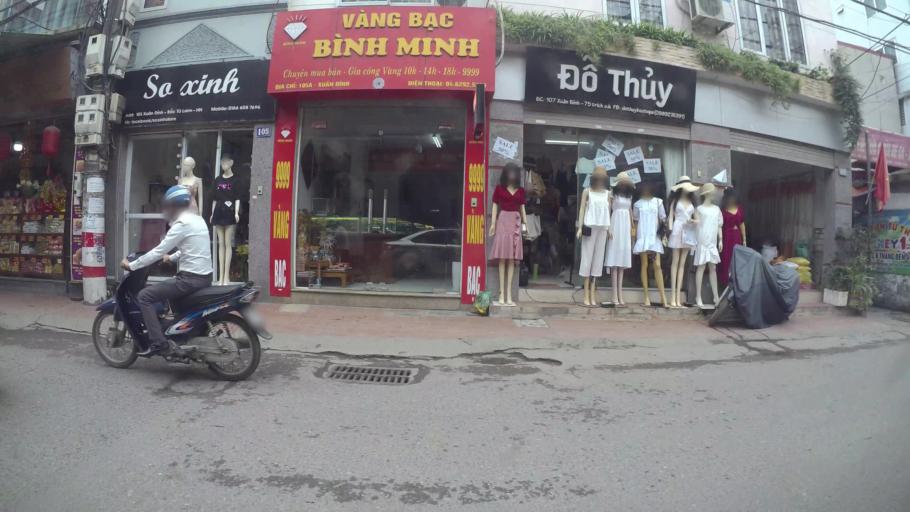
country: VN
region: Ha Noi
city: Tay Ho
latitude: 21.0708
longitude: 105.8003
